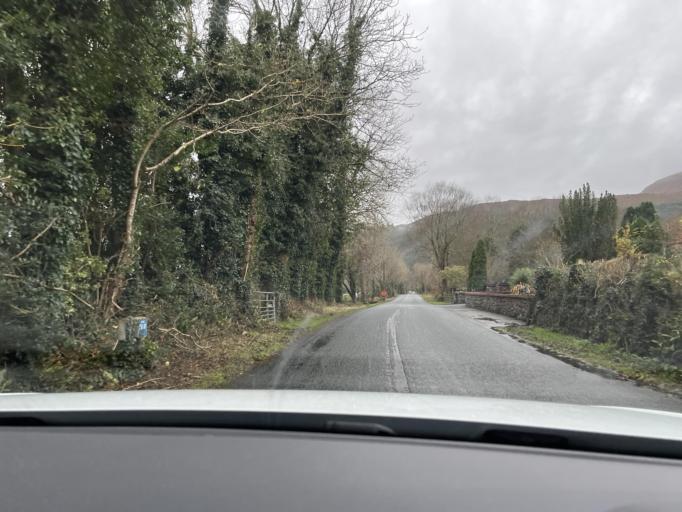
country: IE
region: Connaught
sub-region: County Leitrim
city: Manorhamilton
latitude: 54.2922
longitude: -8.2024
